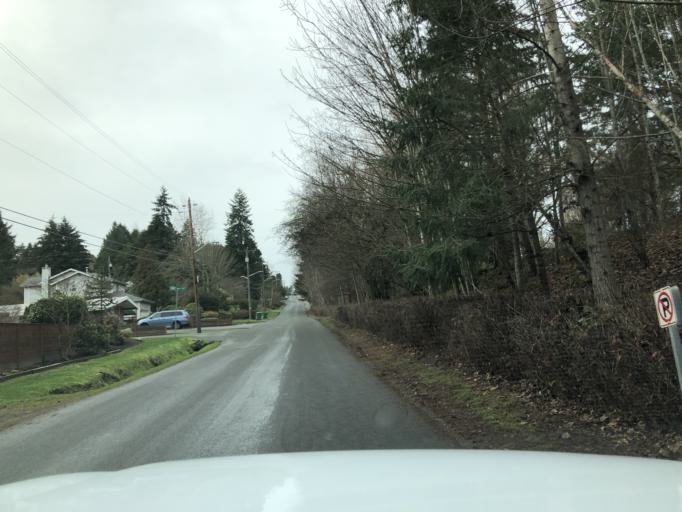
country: US
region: Washington
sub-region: King County
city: Lake Forest Park
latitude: 47.7047
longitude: -122.2876
